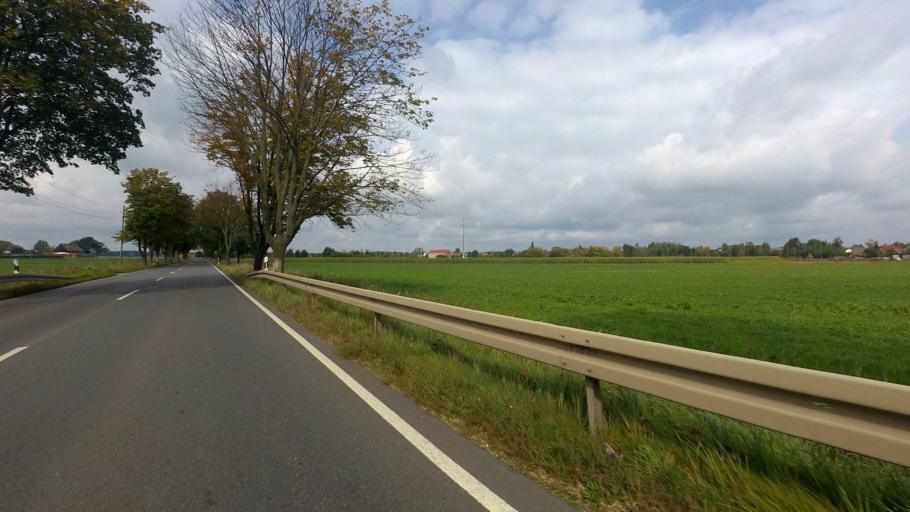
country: DE
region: Brandenburg
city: Tettau
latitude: 51.4660
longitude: 13.7367
